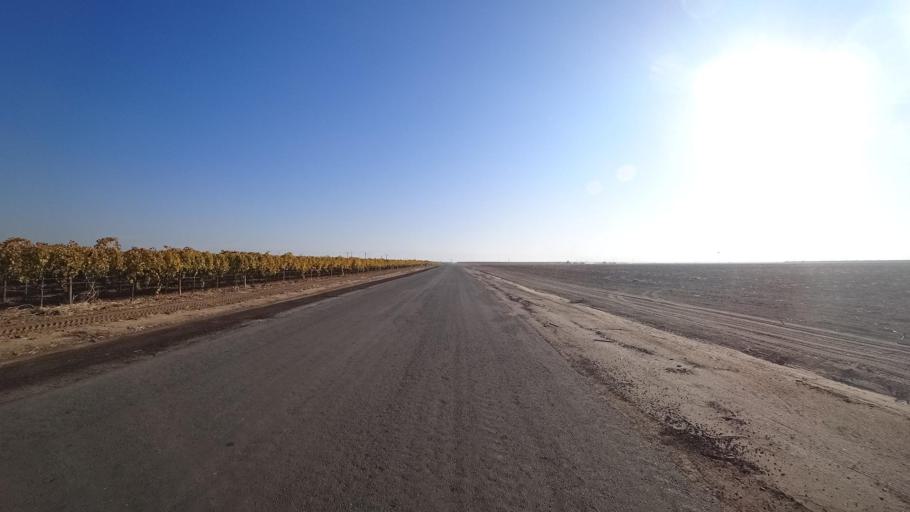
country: US
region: California
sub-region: Tulare County
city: Richgrove
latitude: 35.7687
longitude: -119.1648
